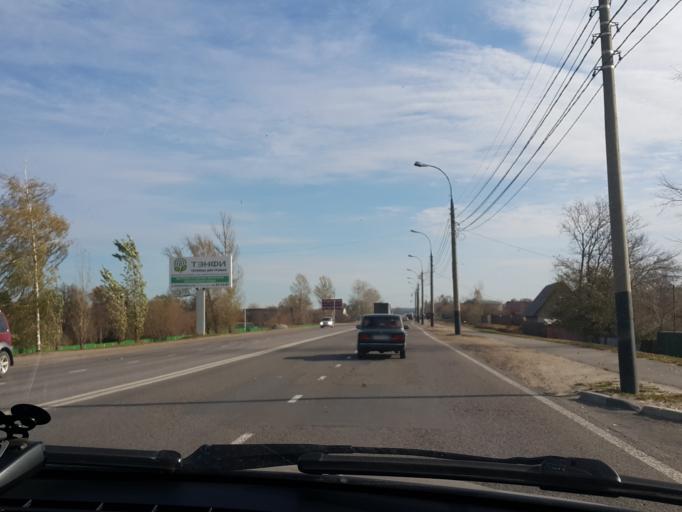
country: RU
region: Tambov
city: Tambov
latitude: 52.7238
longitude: 41.4720
